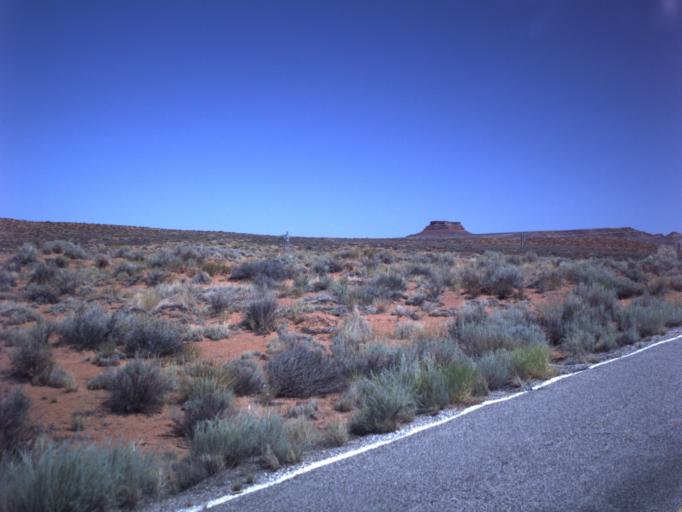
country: US
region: Utah
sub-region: San Juan County
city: Blanding
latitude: 37.1993
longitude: -109.8807
